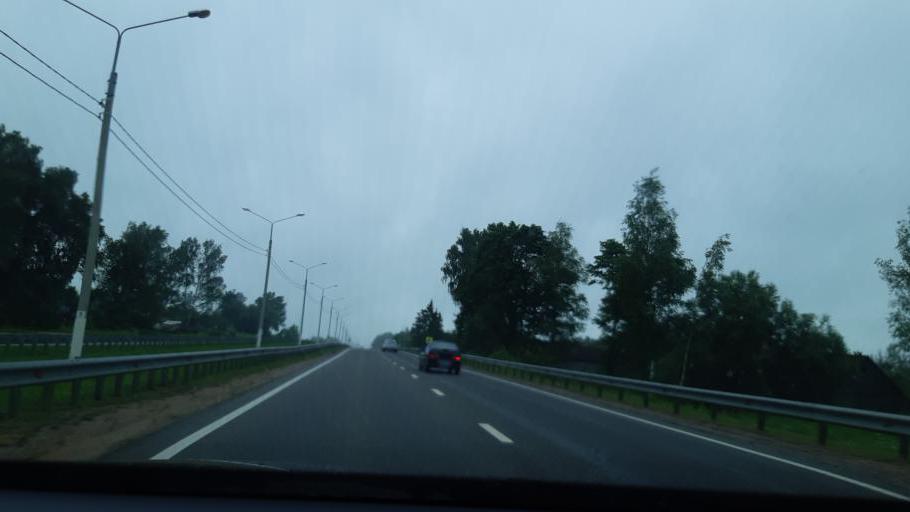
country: RU
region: Smolensk
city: Talashkino
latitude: 54.6715
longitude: 32.1492
